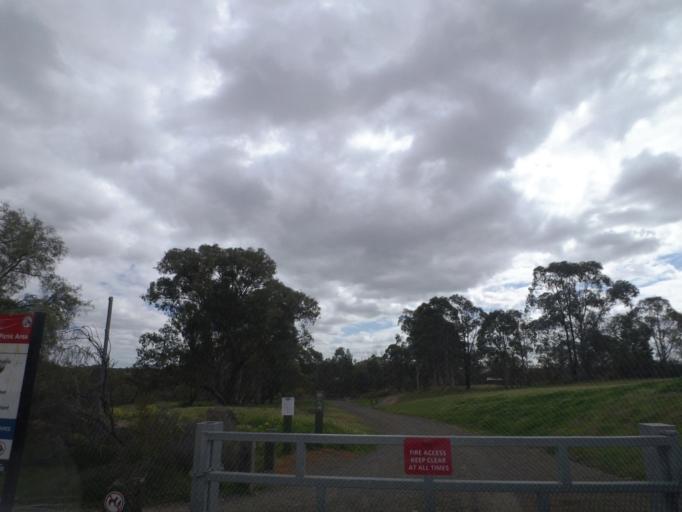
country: AU
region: Victoria
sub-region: Whittlesea
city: Mill Park
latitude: -37.6704
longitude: 145.0896
